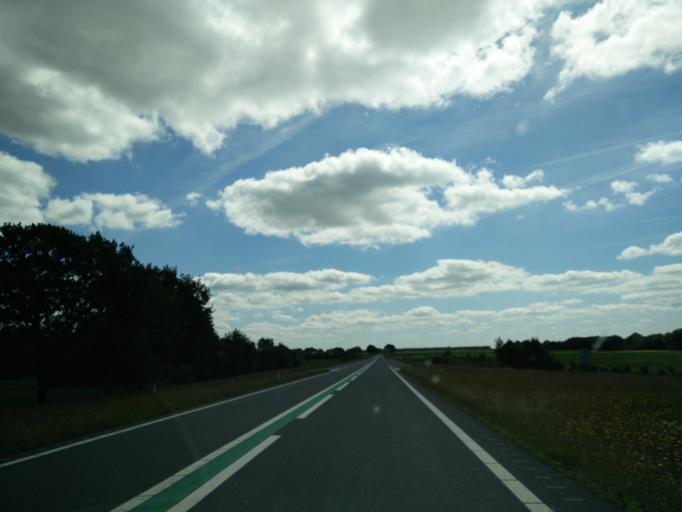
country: NL
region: Drenthe
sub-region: Gemeente Hoogeveen
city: Hoogeveen
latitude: 52.8309
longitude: 6.6079
